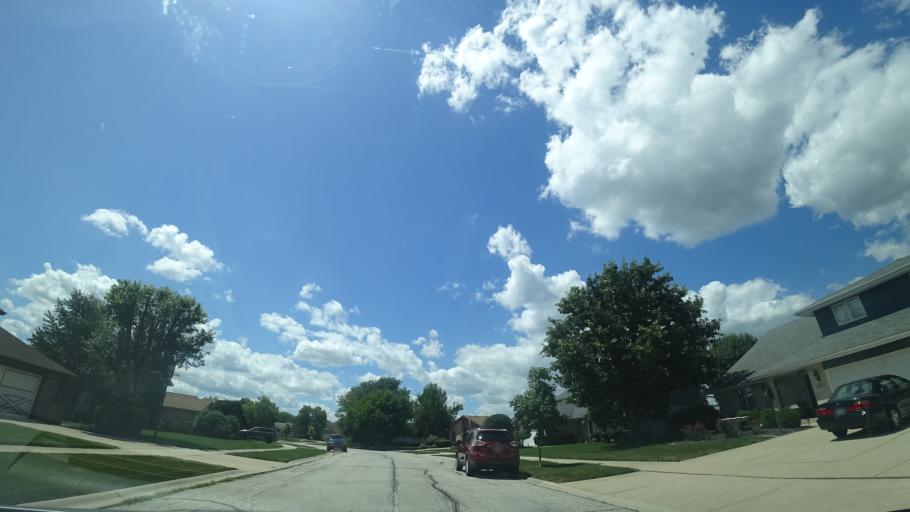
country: US
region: Illinois
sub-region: Will County
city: Homer Glen
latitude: 41.5783
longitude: -87.9008
